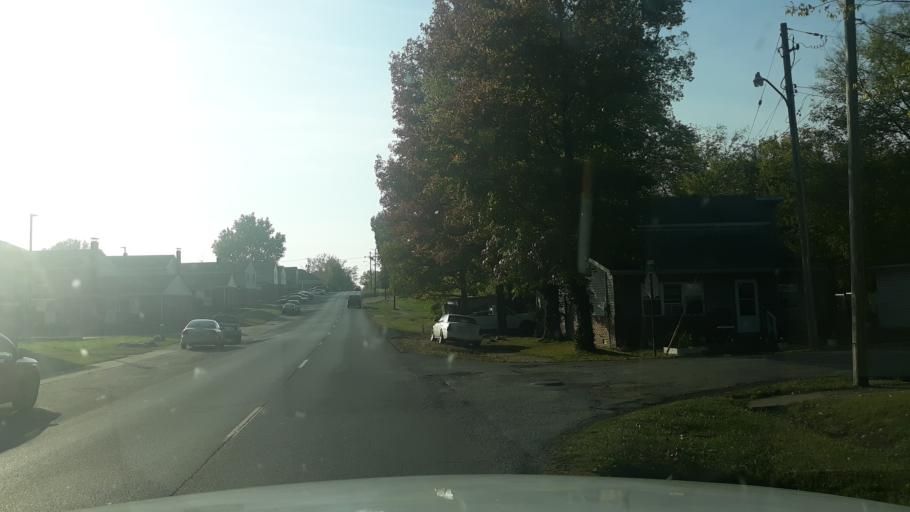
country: US
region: Illinois
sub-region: Saline County
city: Harrisburg
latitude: 37.7203
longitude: -88.5500
